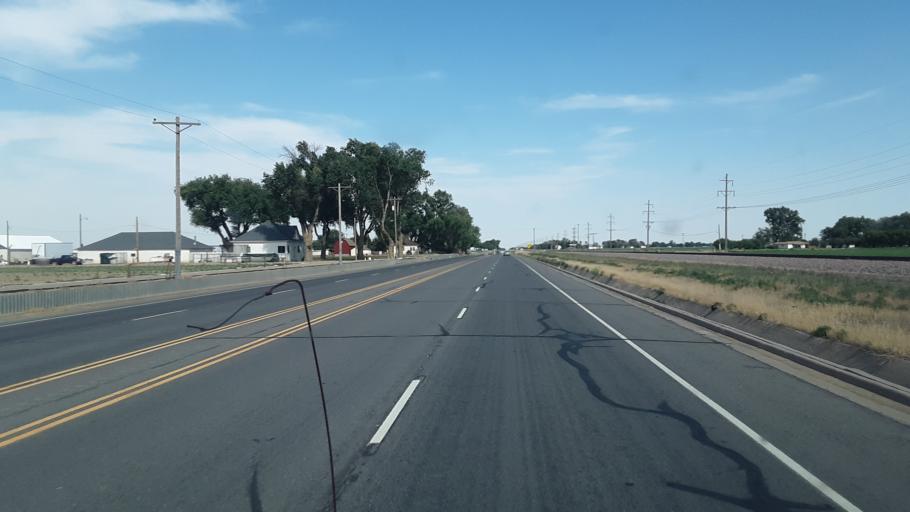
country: US
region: Colorado
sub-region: Otero County
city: Rocky Ford
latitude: 38.0735
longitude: -103.7708
